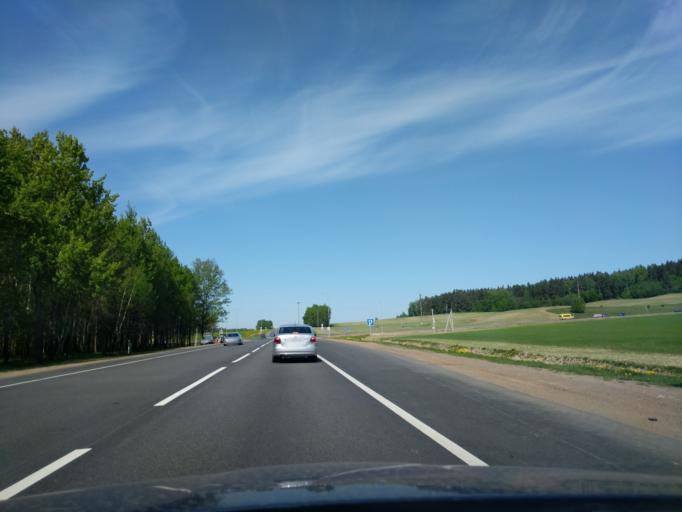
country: BY
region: Minsk
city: Bal'shavik
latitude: 54.0890
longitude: 27.5375
